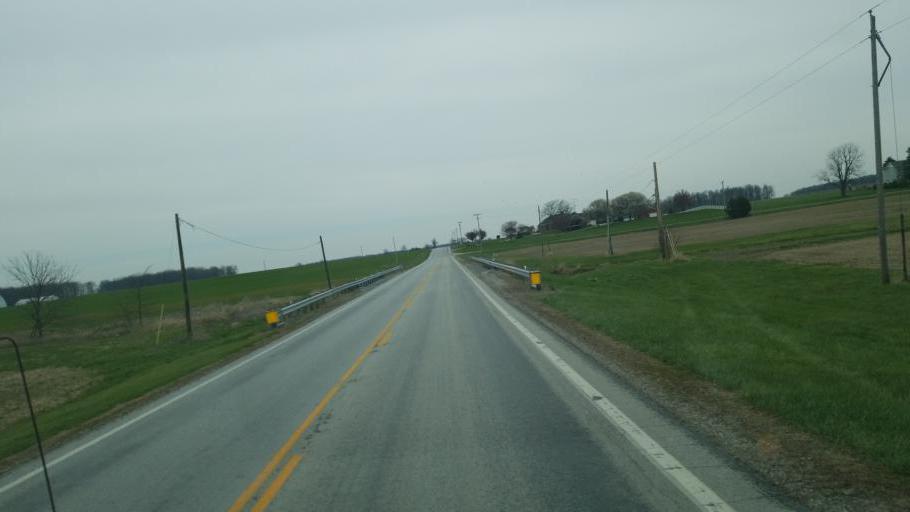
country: US
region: Ohio
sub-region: Hardin County
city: Forest
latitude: 40.8713
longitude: -83.5247
